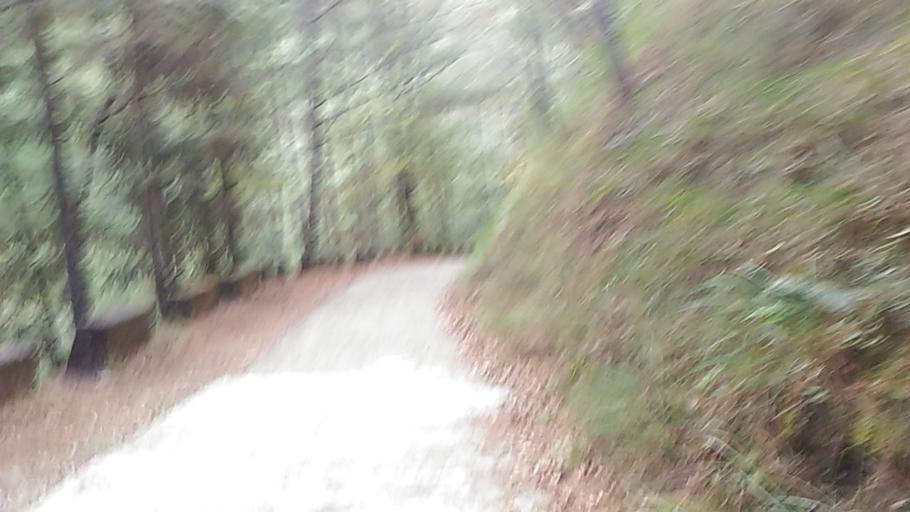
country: TW
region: Taiwan
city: Daxi
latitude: 24.4057
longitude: 121.3036
